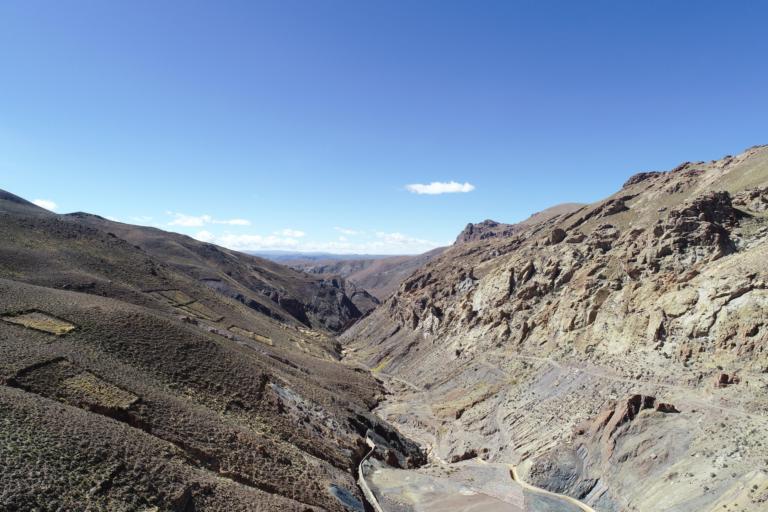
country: BO
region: Potosi
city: Atocha
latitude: -21.1706
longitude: -66.1434
